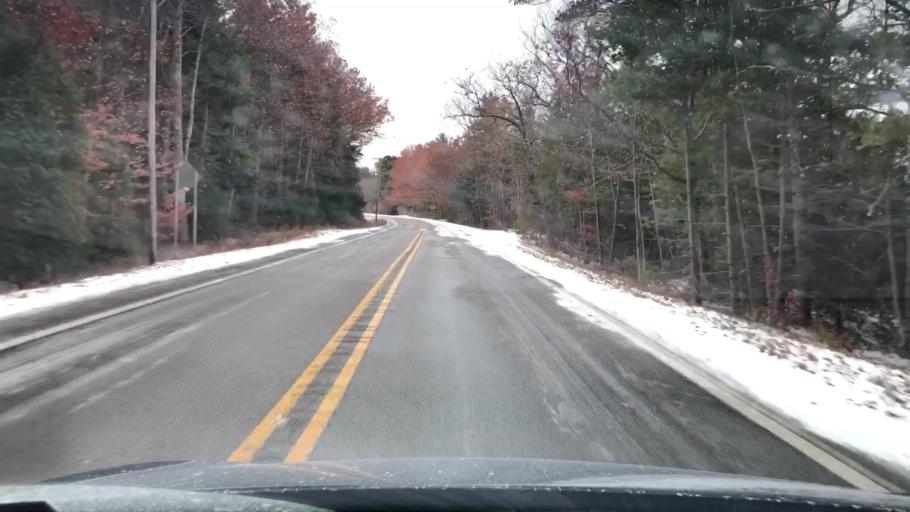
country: US
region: Michigan
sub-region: Antrim County
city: Elk Rapids
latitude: 44.9807
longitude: -85.5000
